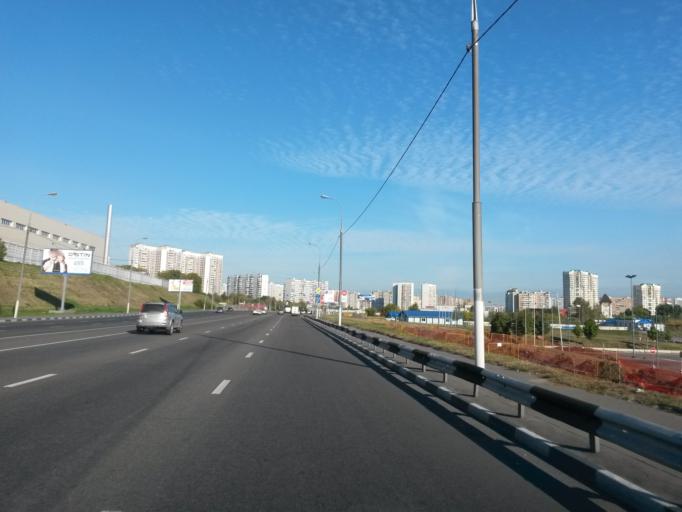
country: RU
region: Moscow
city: Zyablikovo
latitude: 55.6242
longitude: 37.7583
